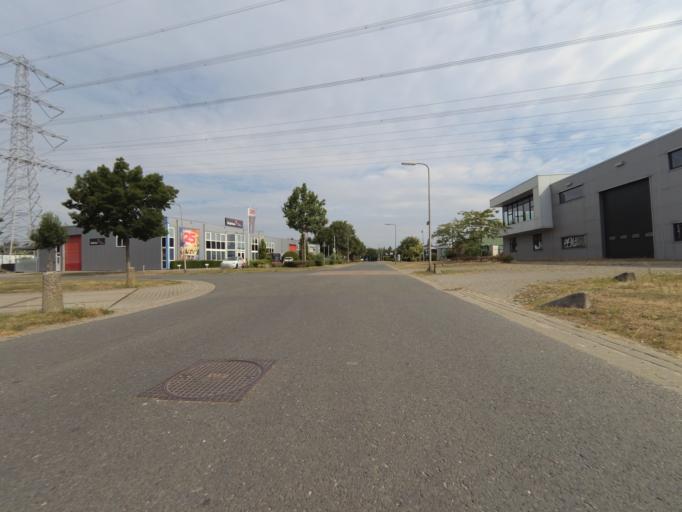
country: NL
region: Overijssel
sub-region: Gemeente Hengelo
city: Hengelo
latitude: 52.2140
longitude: 6.8143
